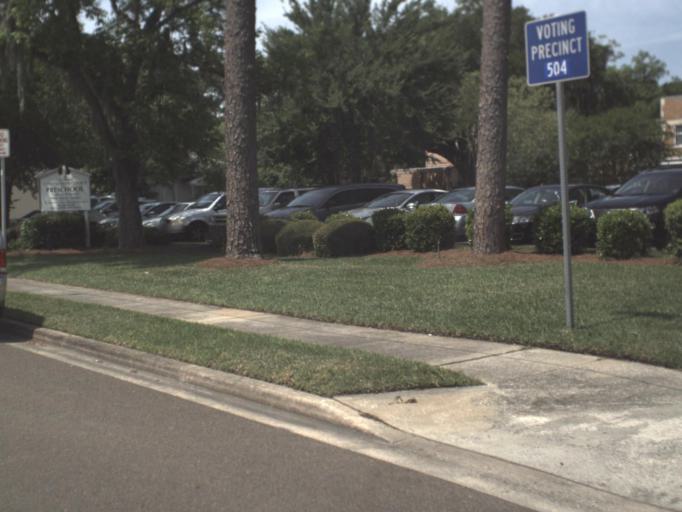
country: US
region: Florida
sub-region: Duval County
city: Jacksonville
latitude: 30.2923
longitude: -81.6484
